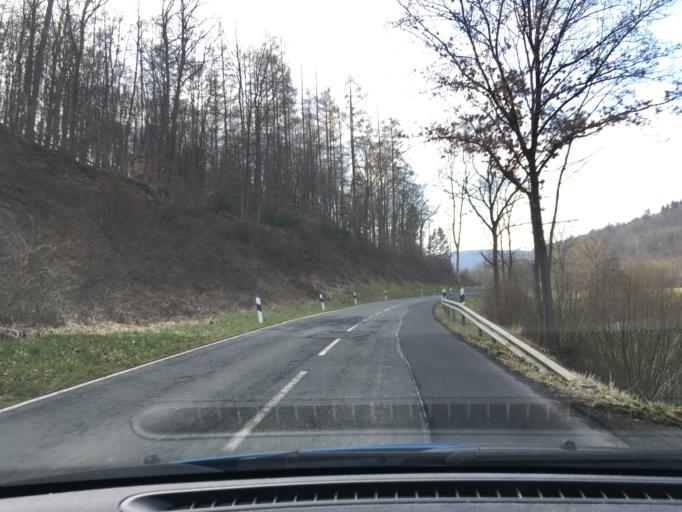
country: DE
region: Lower Saxony
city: Uslar
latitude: 51.6197
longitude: 9.6484
